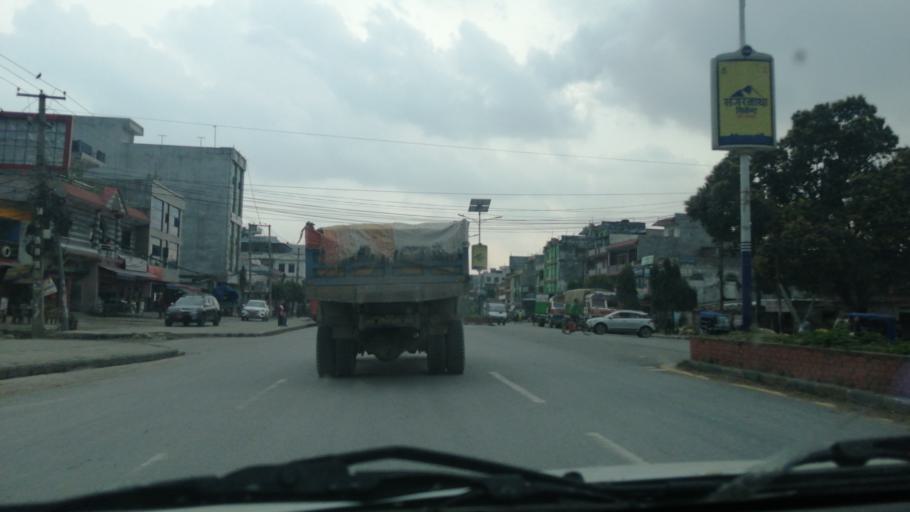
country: NP
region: Western Region
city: Butwal
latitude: 27.7069
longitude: 83.4676
